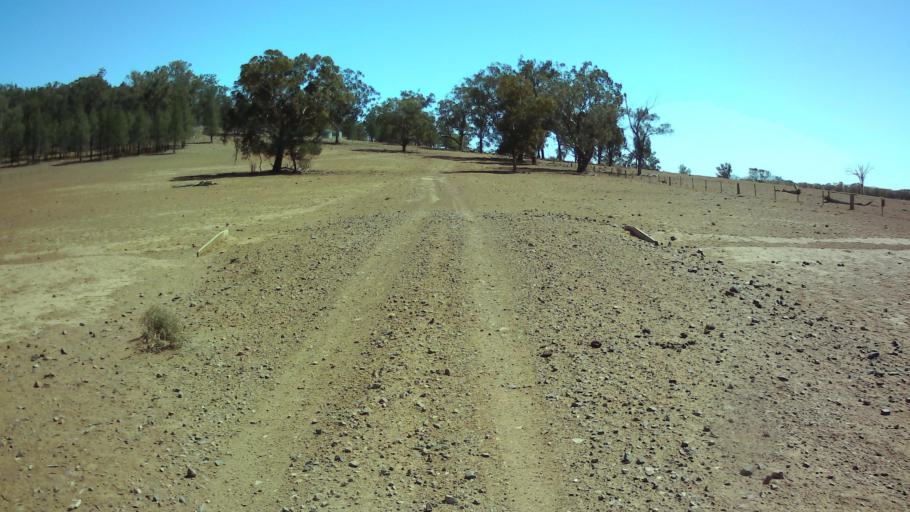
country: AU
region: New South Wales
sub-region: Forbes
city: Forbes
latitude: -33.7338
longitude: 147.6639
